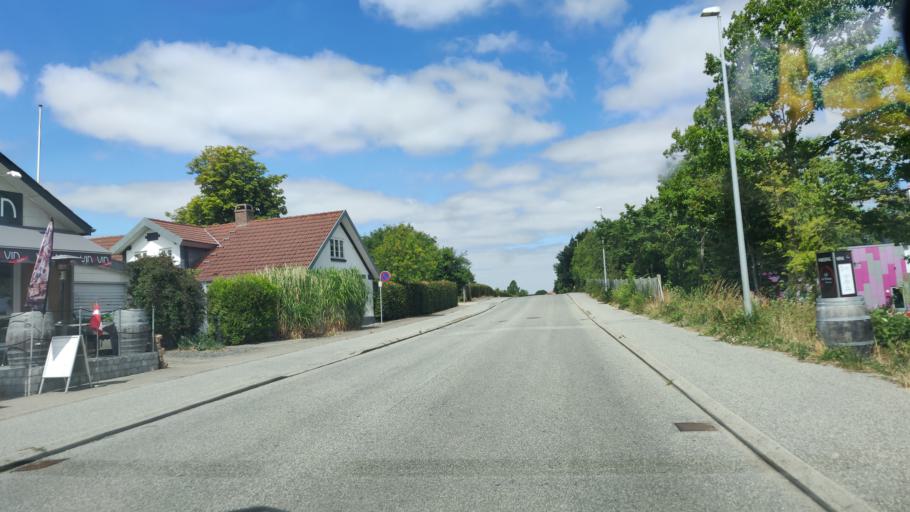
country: DK
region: South Denmark
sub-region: Fredericia Kommune
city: Taulov
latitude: 55.5343
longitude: 9.6207
